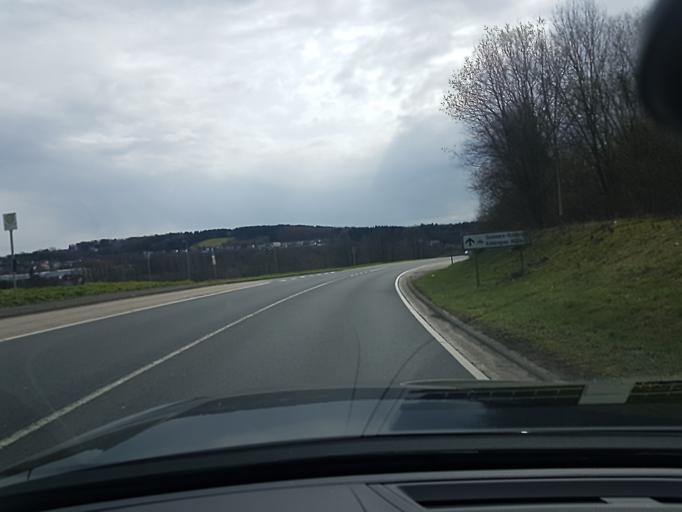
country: DE
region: North Rhine-Westphalia
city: Iserlohn
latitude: 51.4195
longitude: 7.6904
